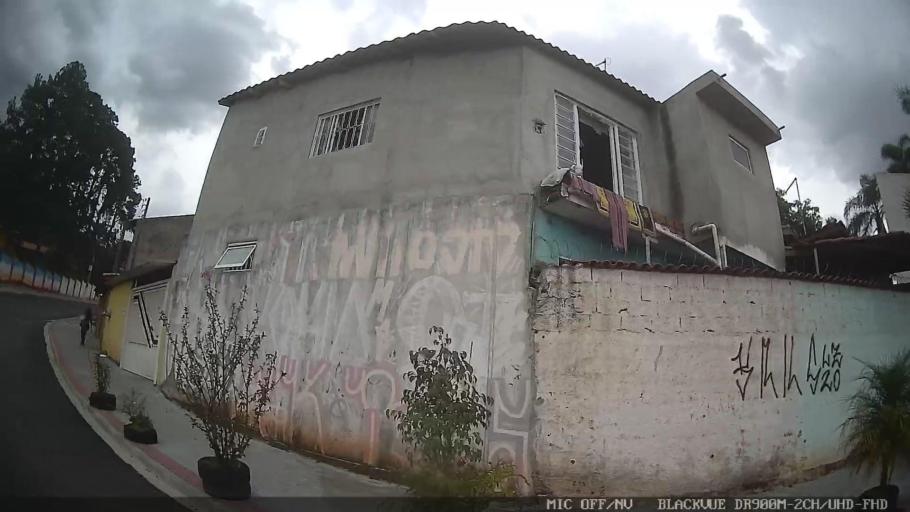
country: BR
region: Sao Paulo
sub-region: Poa
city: Poa
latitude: -23.5399
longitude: -46.3475
